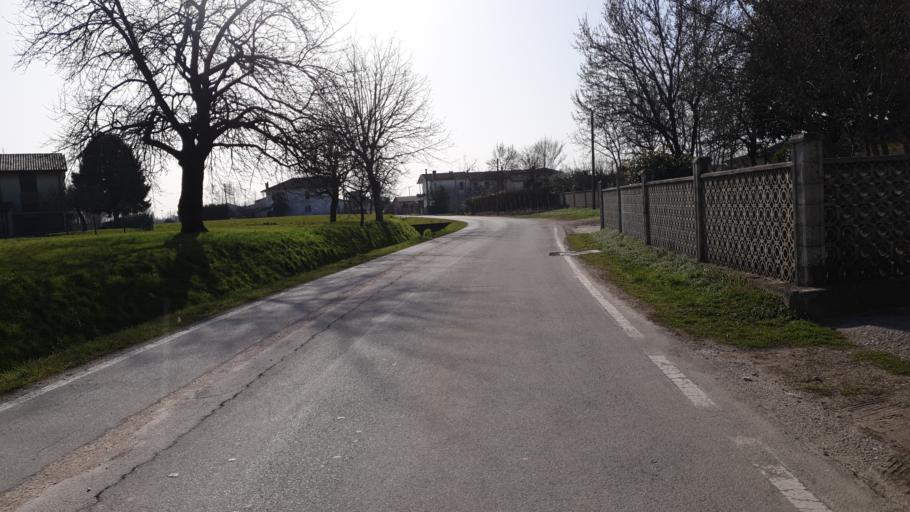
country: IT
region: Veneto
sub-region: Provincia di Padova
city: Cavino
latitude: 45.5050
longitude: 11.8805
